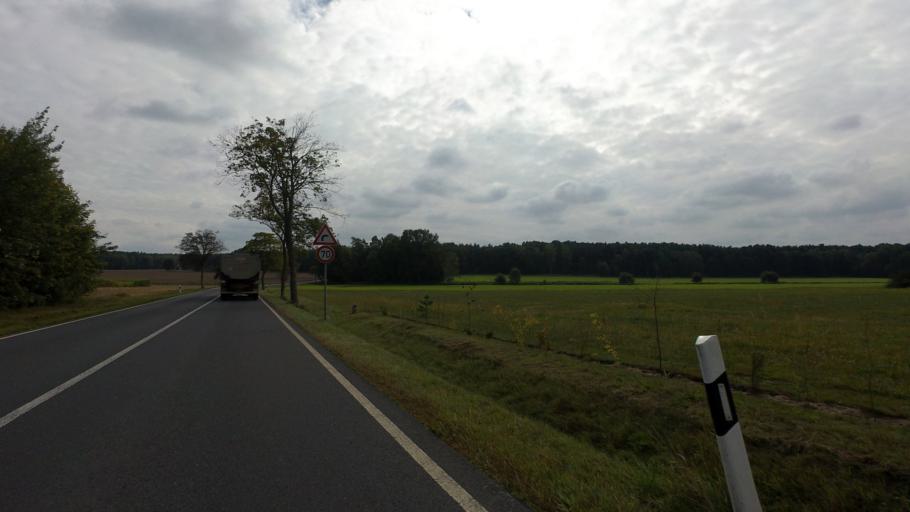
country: DE
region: Brandenburg
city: Kasel-Golzig
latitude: 51.8960
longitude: 13.6828
